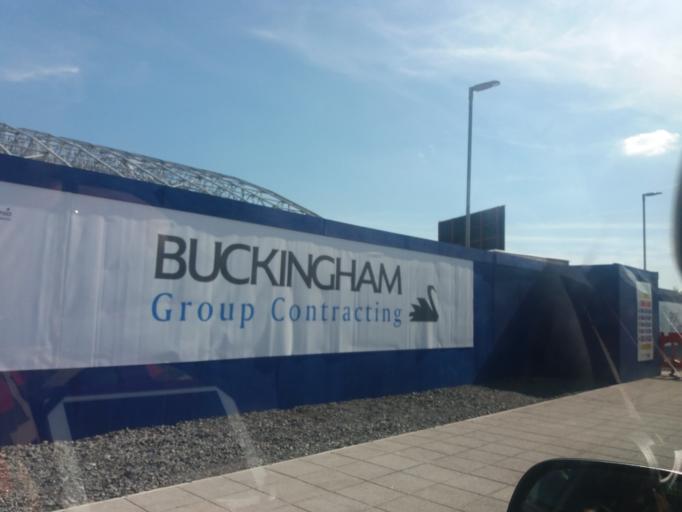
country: IE
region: Leinster
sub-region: Fingal County
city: Blanchardstown
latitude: 53.3977
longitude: -6.3603
